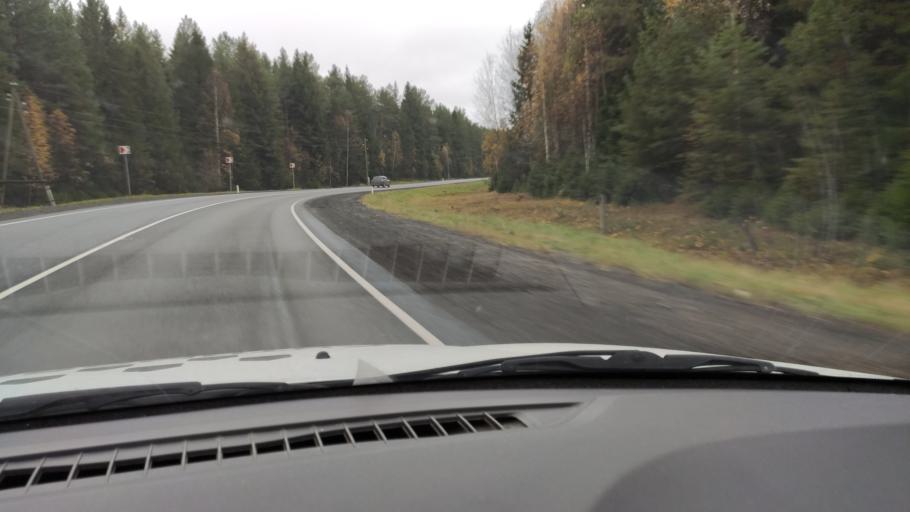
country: RU
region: Kirov
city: Belaya Kholunitsa
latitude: 58.8788
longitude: 50.8692
